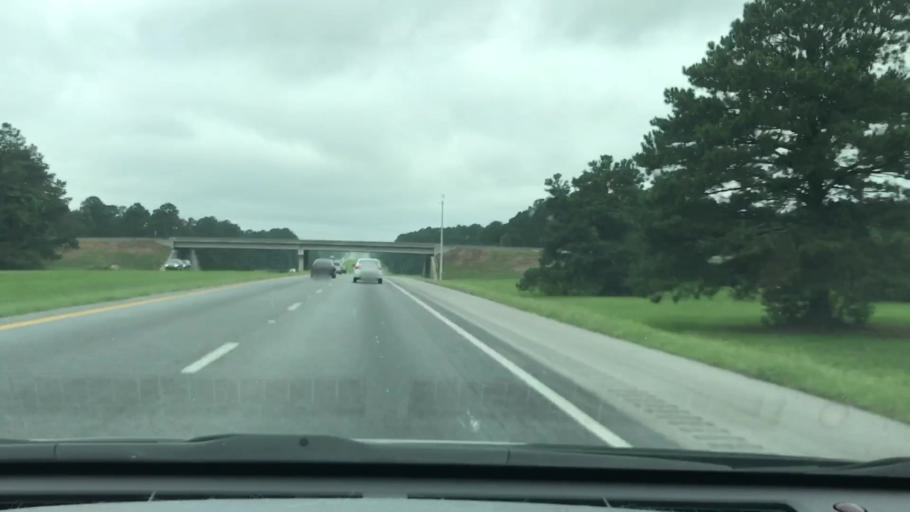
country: US
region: Georgia
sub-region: Walton County
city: Social Circle
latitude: 33.5925
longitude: -83.6284
